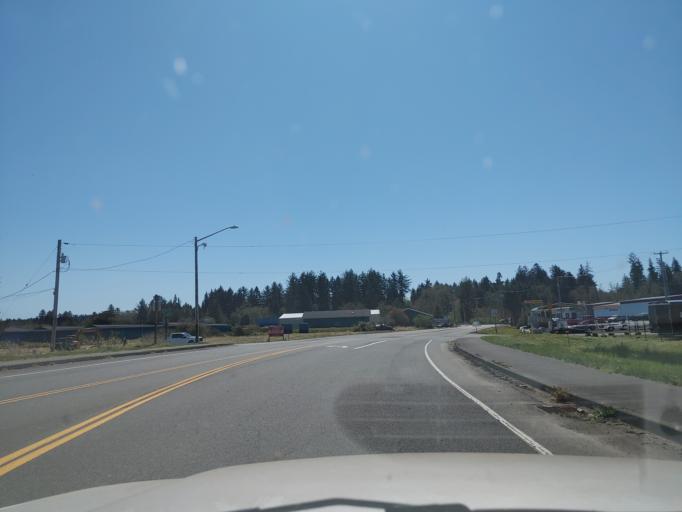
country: US
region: Oregon
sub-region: Clatsop County
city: Warrenton
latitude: 46.1571
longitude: -123.9044
